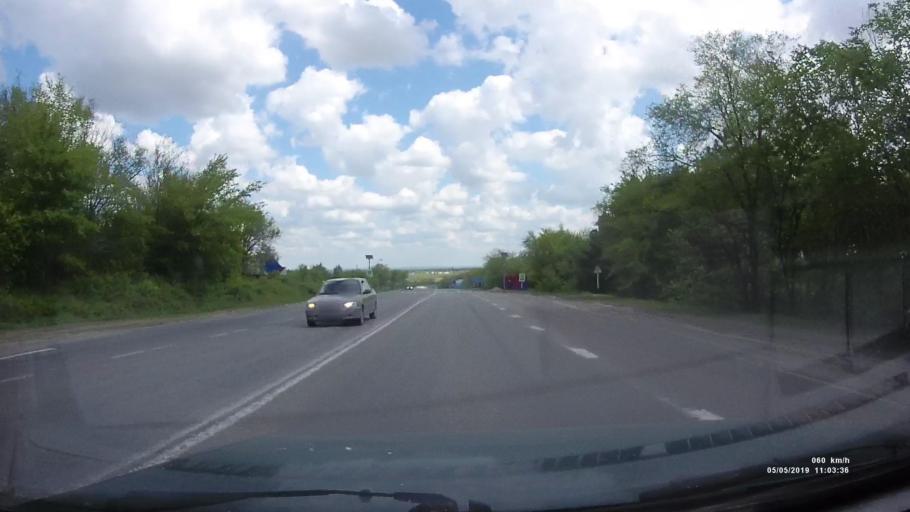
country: RU
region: Rostov
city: Ust'-Donetskiy
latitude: 47.6929
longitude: 40.9221
